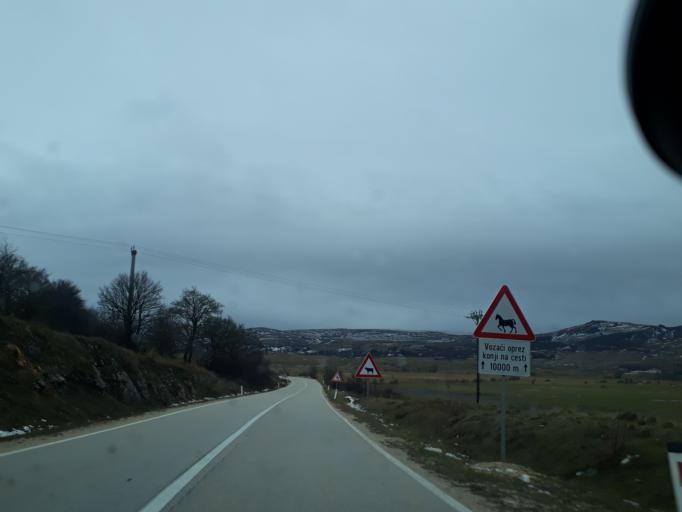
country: BA
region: Federation of Bosnia and Herzegovina
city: Tomislavgrad
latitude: 43.8352
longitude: 17.1875
